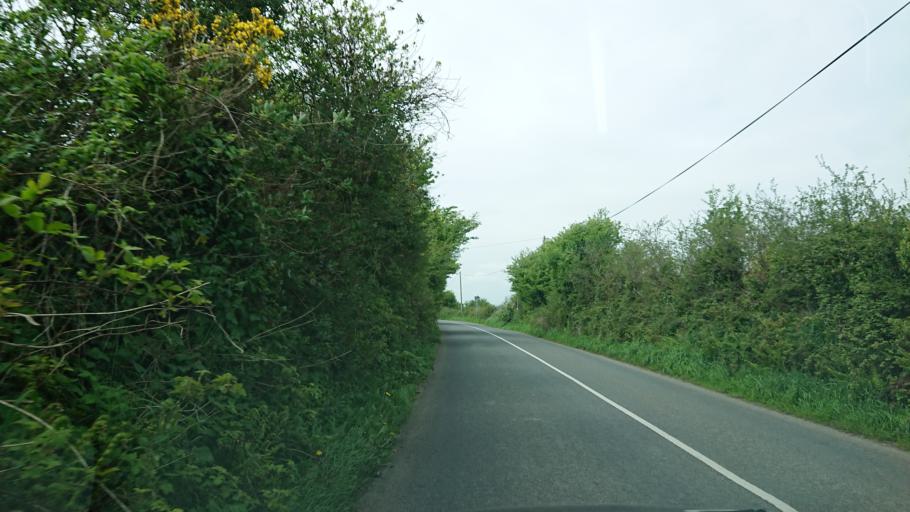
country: IE
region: Munster
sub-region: Waterford
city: Waterford
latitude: 52.2210
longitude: -7.0683
